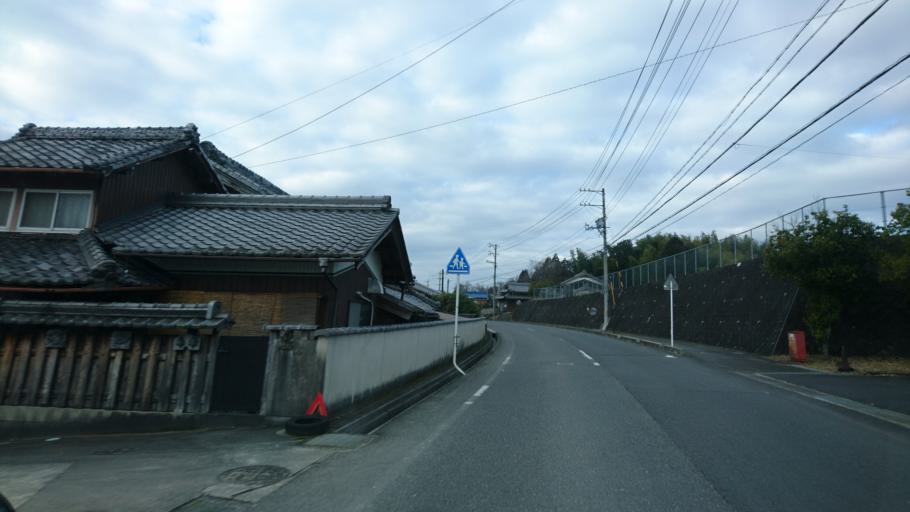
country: JP
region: Mie
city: Ueno-ebisumachi
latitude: 34.7336
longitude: 136.0964
